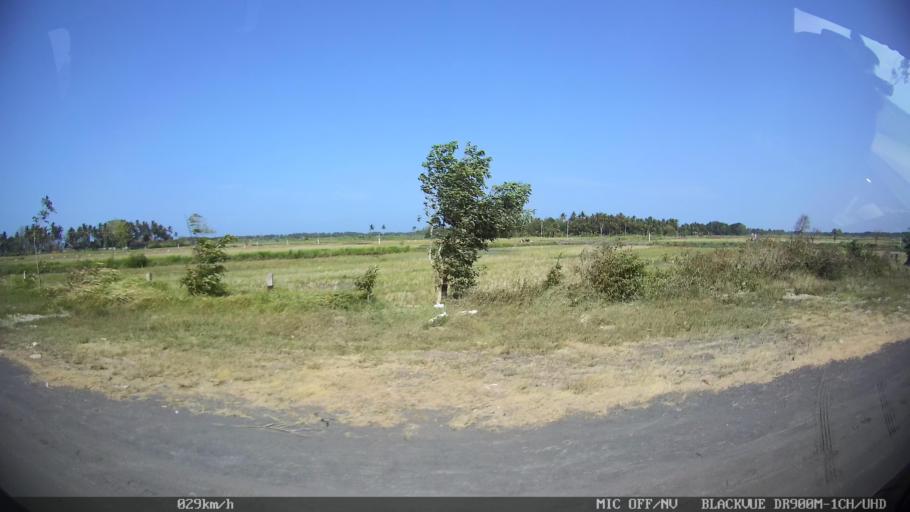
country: ID
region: Daerah Istimewa Yogyakarta
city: Srandakan
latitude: -7.9711
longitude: 110.2089
